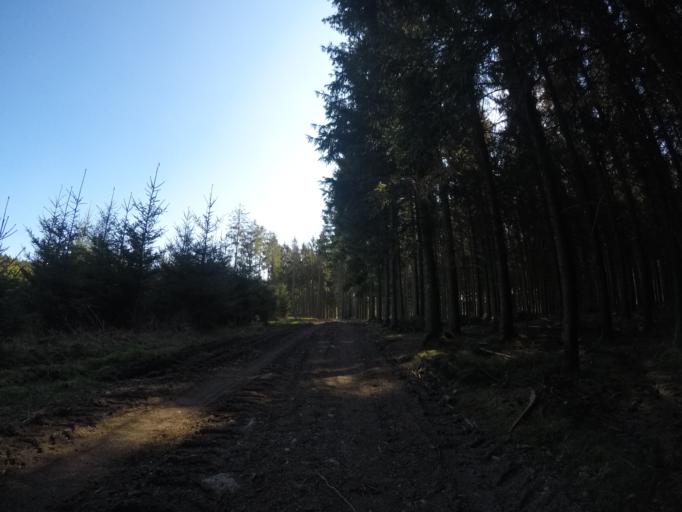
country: BE
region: Wallonia
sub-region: Province du Luxembourg
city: Leglise
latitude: 49.8008
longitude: 5.5908
